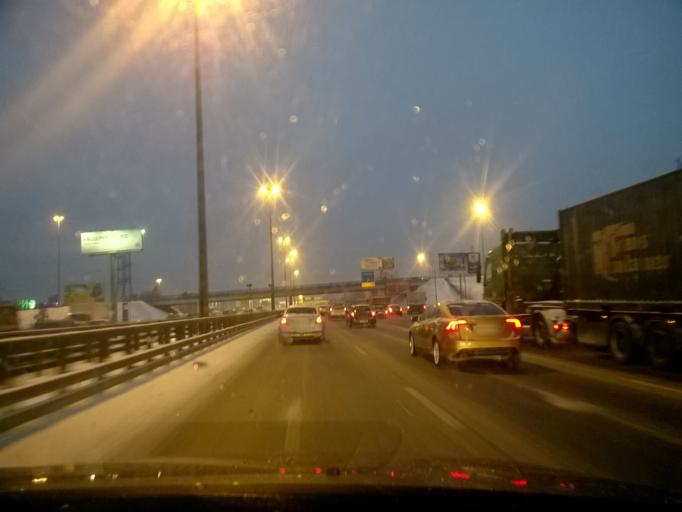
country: RU
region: Moscow
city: Solntsevo
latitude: 55.6266
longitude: 37.4214
